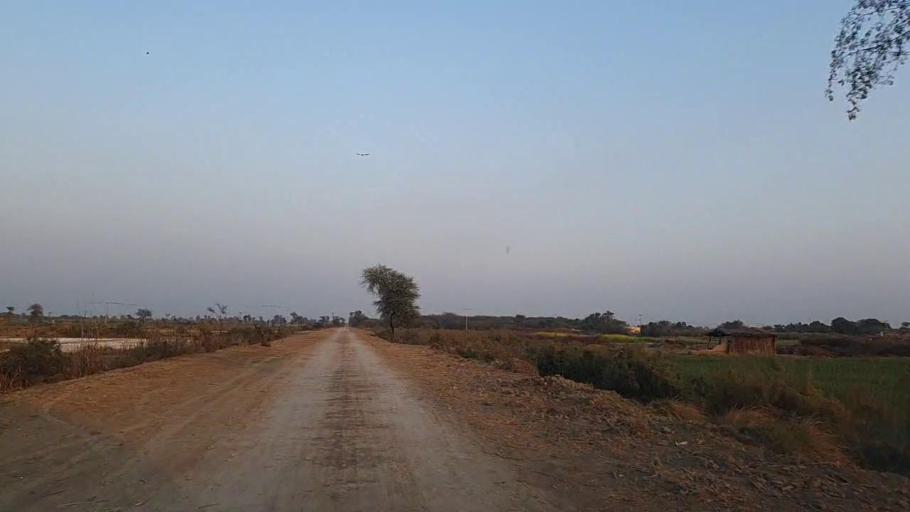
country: PK
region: Sindh
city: Jam Sahib
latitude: 26.3049
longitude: 68.5738
